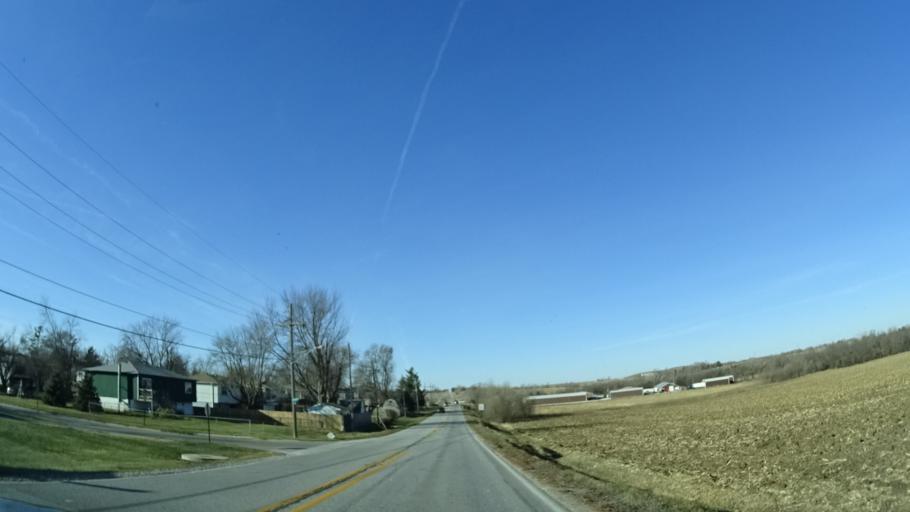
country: US
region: Nebraska
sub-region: Sarpy County
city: Springfield
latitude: 41.0891
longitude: -96.1290
